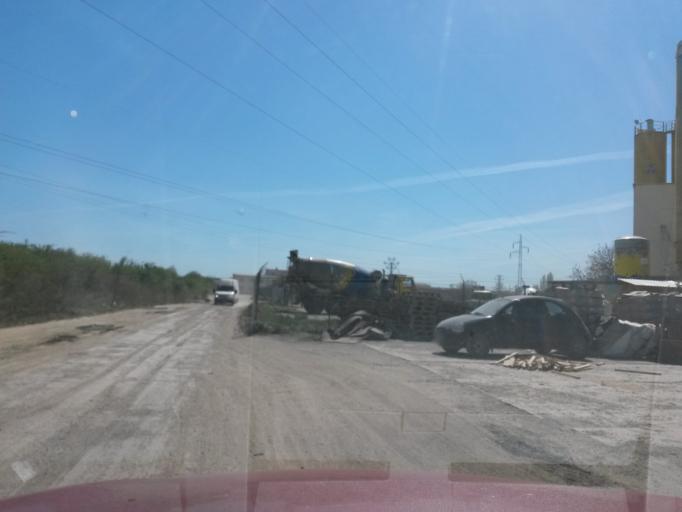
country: SK
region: Kosicky
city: Kosice
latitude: 48.6752
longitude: 21.2762
